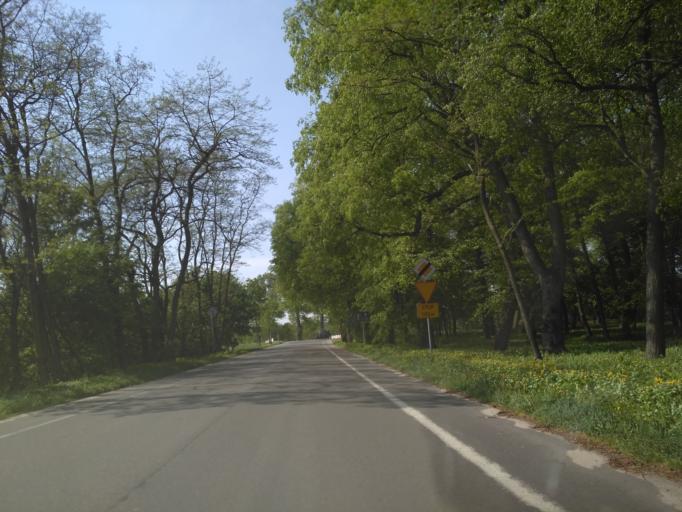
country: PL
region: Lublin Voivodeship
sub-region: Powiat lubartowski
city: Kamionka
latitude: 51.4595
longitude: 22.4858
